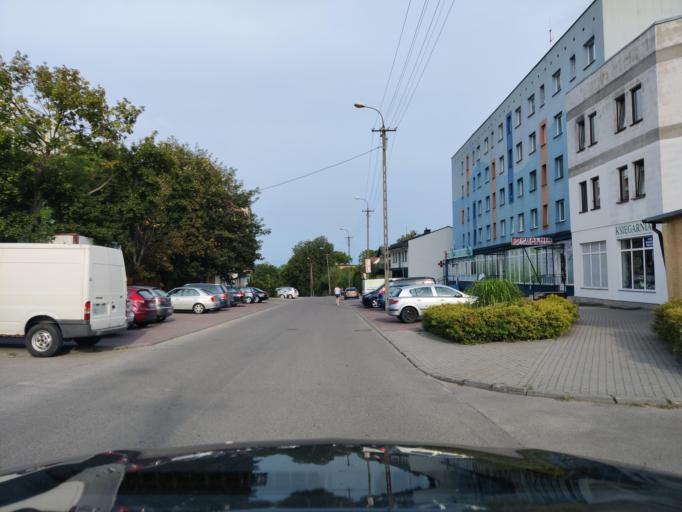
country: PL
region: Masovian Voivodeship
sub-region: Powiat pultuski
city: Pultusk
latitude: 52.7036
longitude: 21.0808
